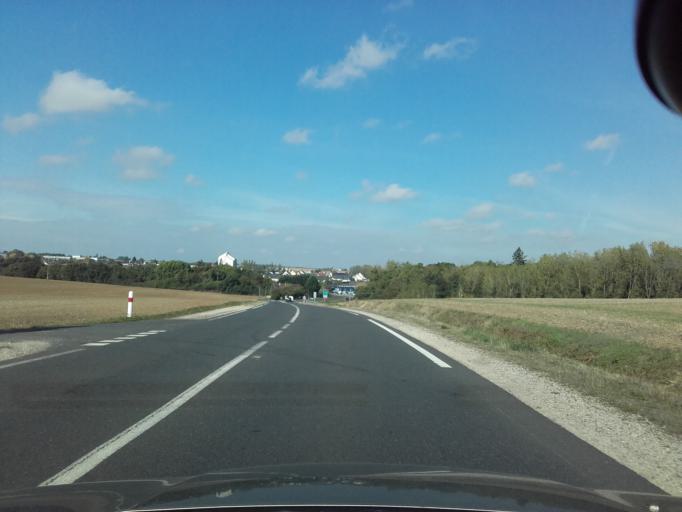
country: FR
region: Centre
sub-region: Departement d'Indre-et-Loire
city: Chateau-Renault
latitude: 47.5931
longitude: 0.9304
